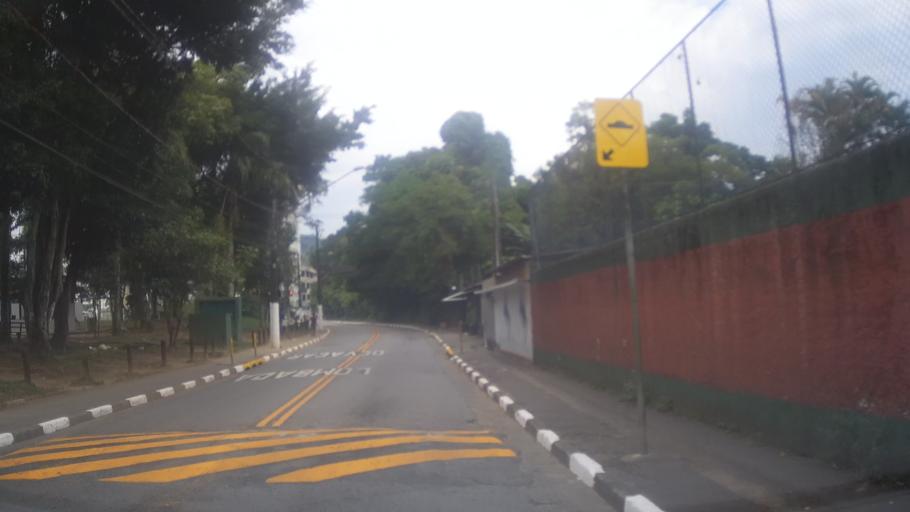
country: BR
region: Sao Paulo
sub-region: Santos
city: Santos
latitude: -23.9470
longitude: -46.3540
